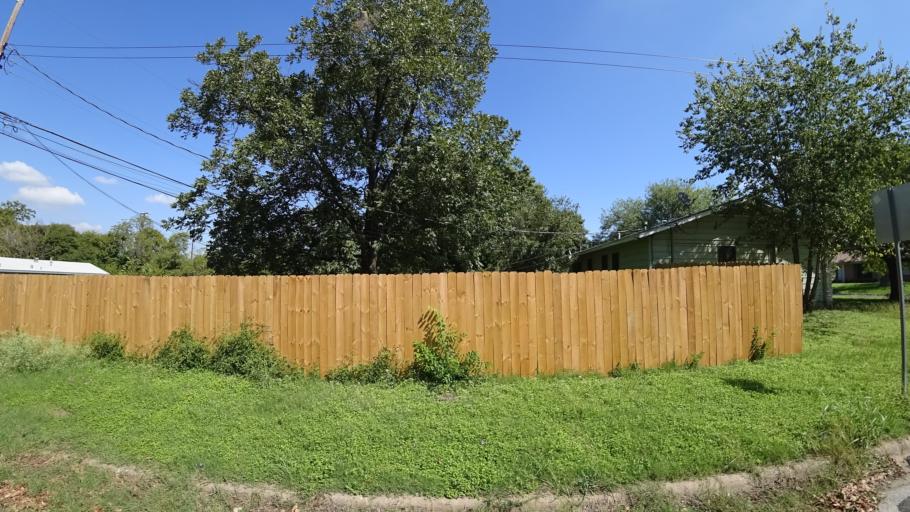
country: US
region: Texas
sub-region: Travis County
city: Austin
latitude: 30.3345
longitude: -97.7133
